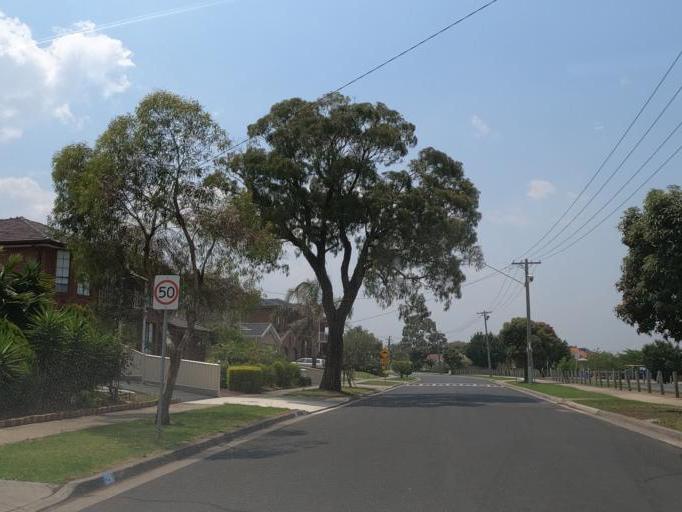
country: AU
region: Victoria
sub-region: Hume
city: Greenvale
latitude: -37.6388
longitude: 144.8874
